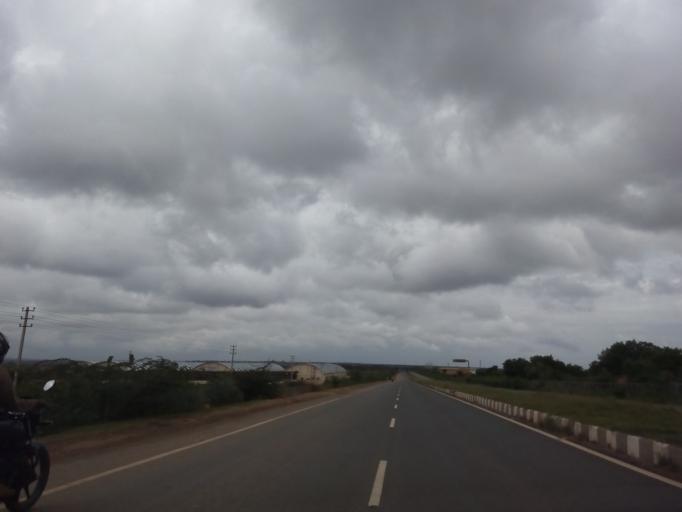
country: IN
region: Karnataka
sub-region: Haveri
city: Ranibennur
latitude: 14.6501
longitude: 75.5716
